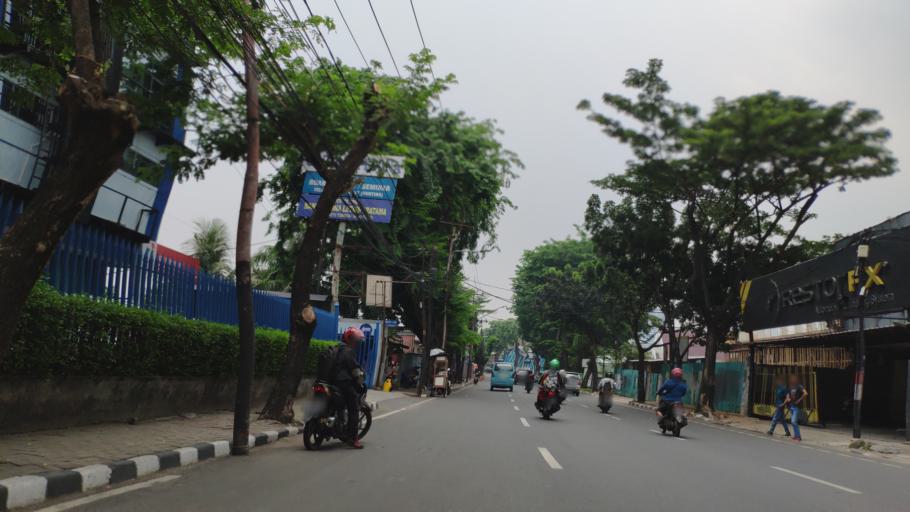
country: ID
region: Banten
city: South Tangerang
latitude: -6.2530
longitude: 106.7778
